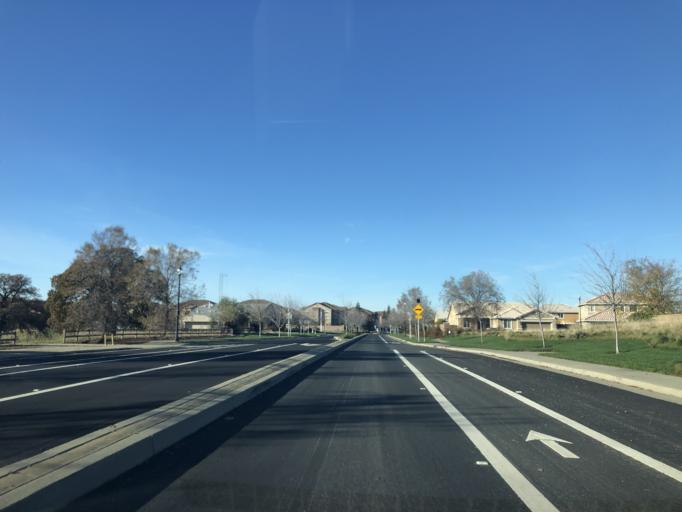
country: US
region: California
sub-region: Sacramento County
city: Antelope
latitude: 38.7880
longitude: -121.3702
